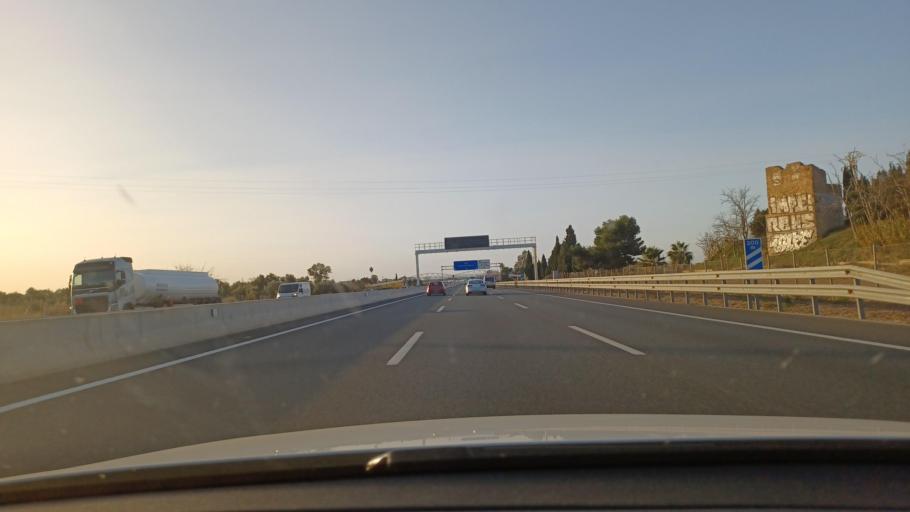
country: ES
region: Valencia
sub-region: Provincia de Valencia
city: Puig
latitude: 39.5922
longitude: -0.2933
